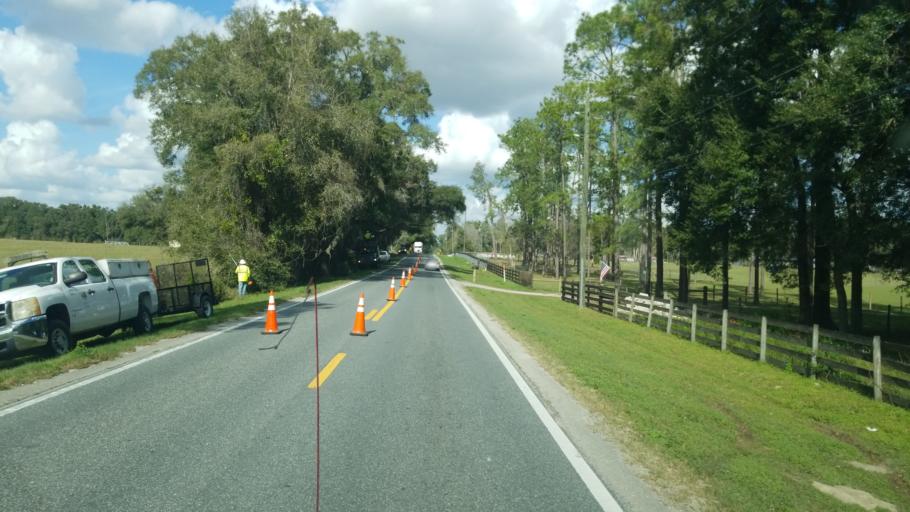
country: US
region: Florida
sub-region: Marion County
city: Belleview
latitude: 29.0005
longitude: -82.1199
